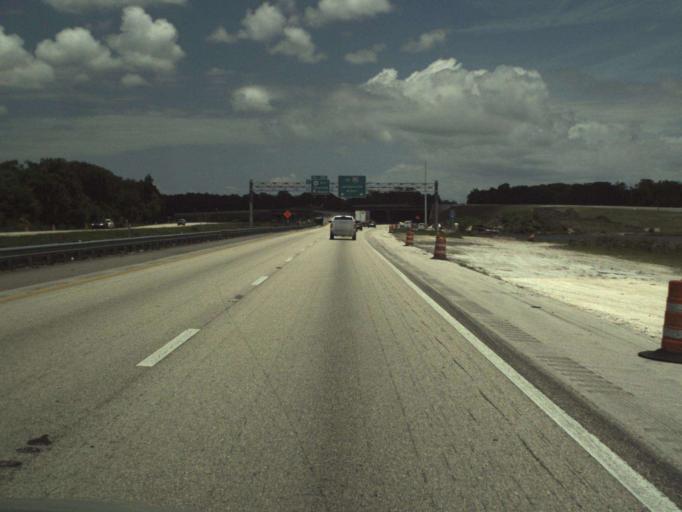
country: US
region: Florida
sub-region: Volusia County
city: Samsula-Spruce Creek
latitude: 29.1330
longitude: -81.1222
